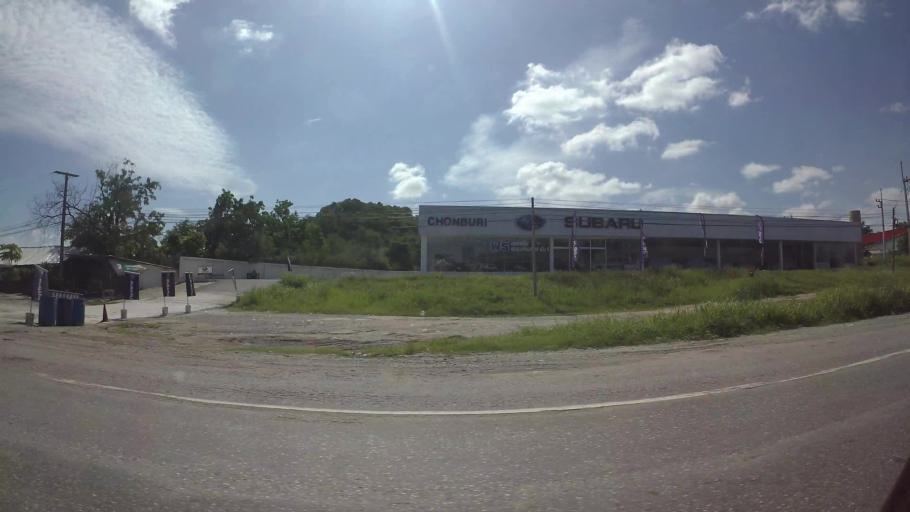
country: TH
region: Chon Buri
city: Chon Buri
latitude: 13.3219
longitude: 100.9911
